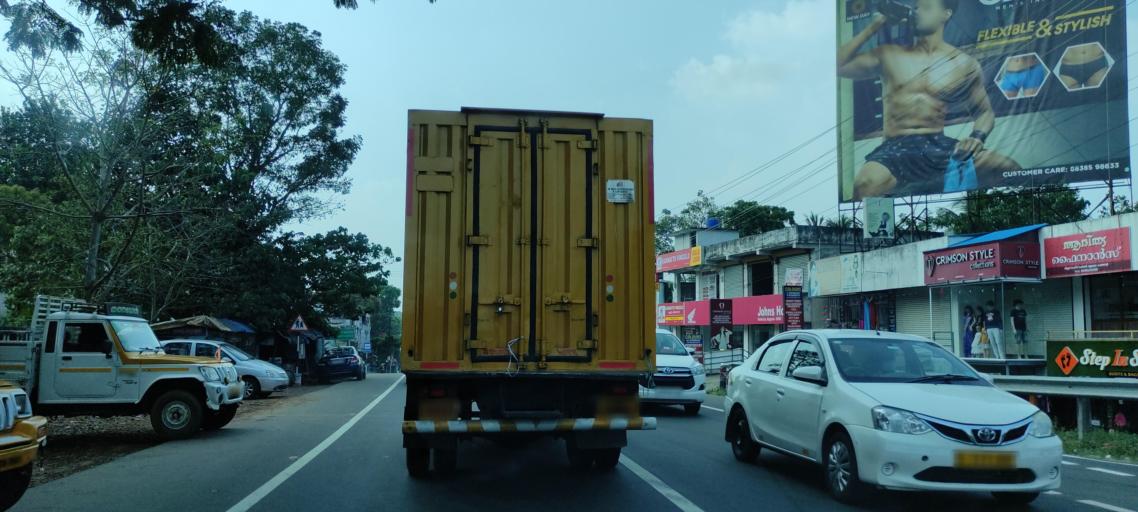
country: IN
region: Kerala
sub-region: Alappuzha
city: Chengannur
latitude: 9.2913
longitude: 76.6488
